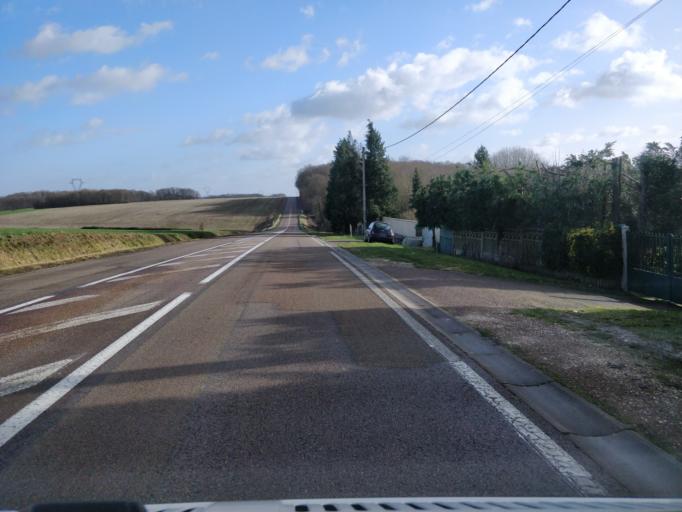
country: FR
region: Bourgogne
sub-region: Departement de l'Yonne
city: Cheroy
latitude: 48.1990
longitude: 3.0162
